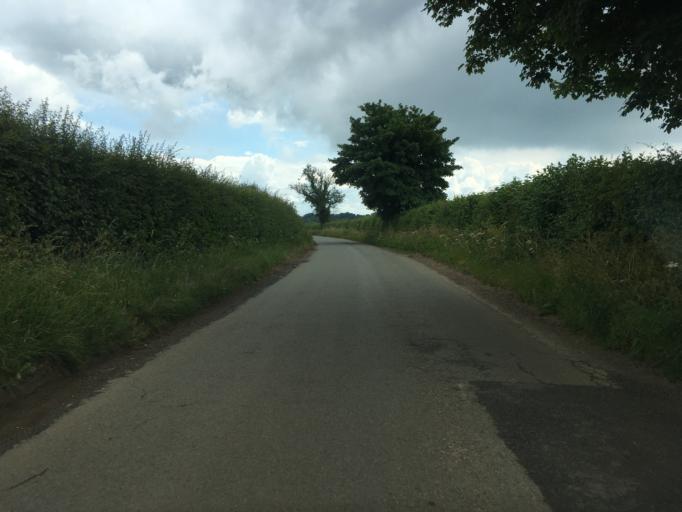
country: GB
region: England
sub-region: Gloucestershire
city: Coates
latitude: 51.7622
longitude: -2.0619
